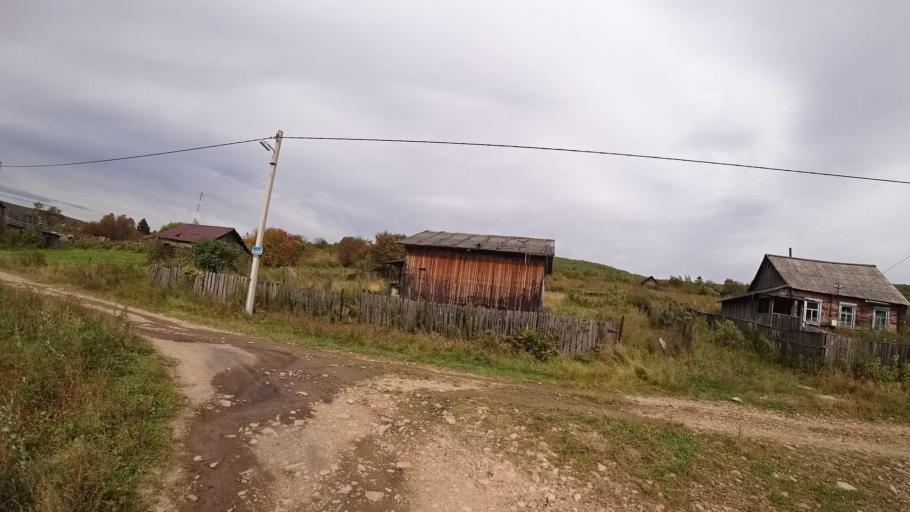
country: RU
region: Jewish Autonomous Oblast
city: Khingansk
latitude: 49.1223
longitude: 131.2078
